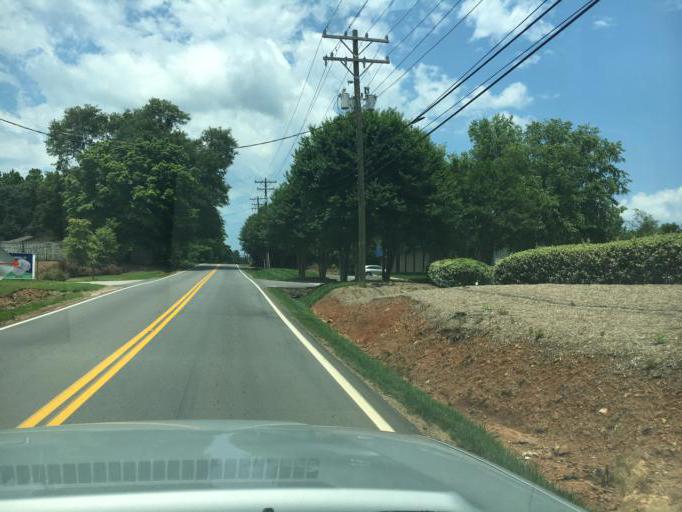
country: US
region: South Carolina
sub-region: Greenville County
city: Five Forks
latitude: 34.8605
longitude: -82.2357
